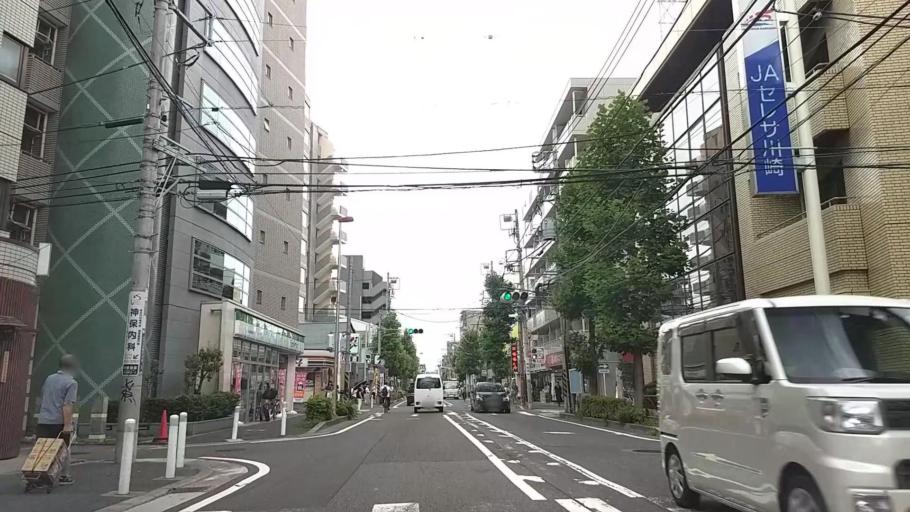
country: JP
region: Kanagawa
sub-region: Kawasaki-shi
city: Kawasaki
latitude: 35.5802
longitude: 139.6417
